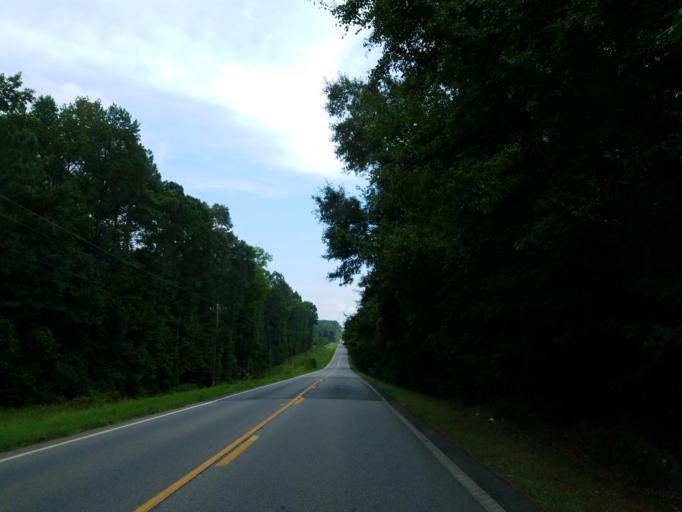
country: US
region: Georgia
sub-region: Dooly County
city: Unadilla
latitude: 32.3281
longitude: -83.7364
